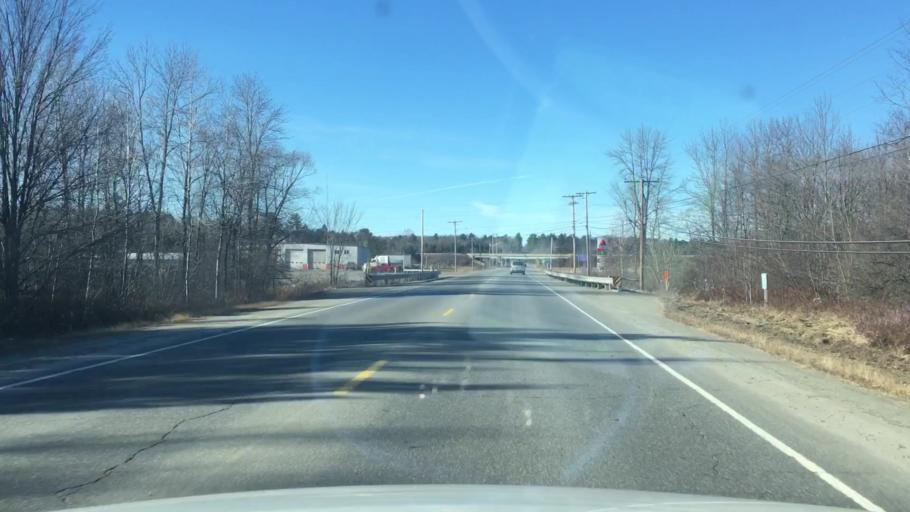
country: US
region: Maine
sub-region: Kennebec County
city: Clinton
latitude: 44.6390
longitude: -69.5219
